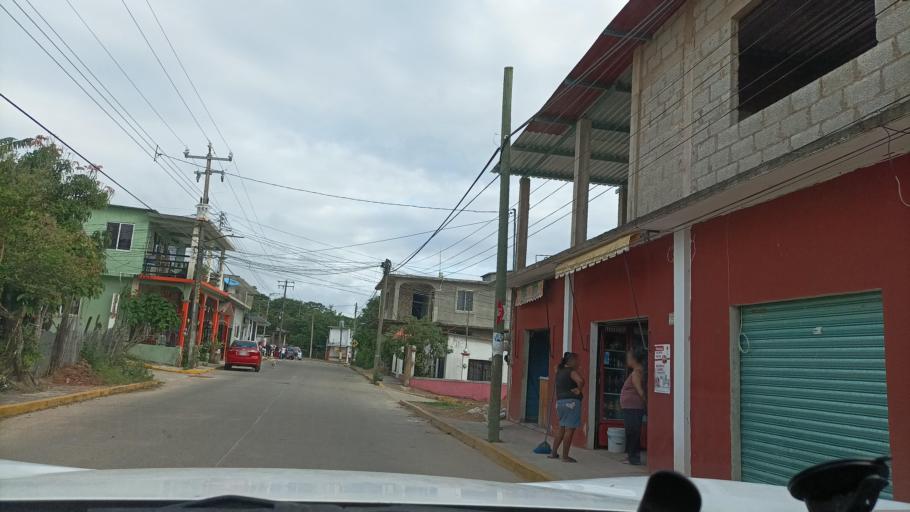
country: MX
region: Veracruz
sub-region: Cosoleacaque
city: Hermenegildo J. Aldana
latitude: 17.9964
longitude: -94.6113
